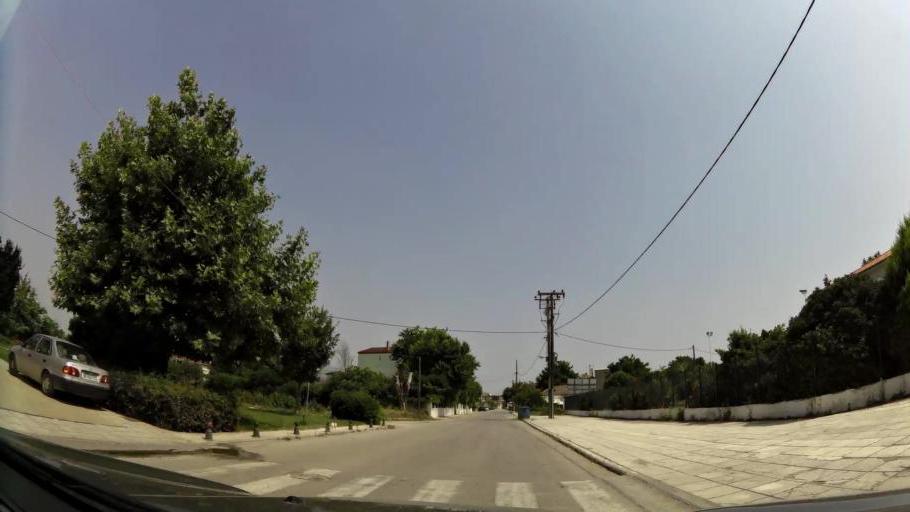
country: GR
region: Central Macedonia
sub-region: Nomos Thessalonikis
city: Nea Magnisia
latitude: 40.6876
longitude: 22.8367
